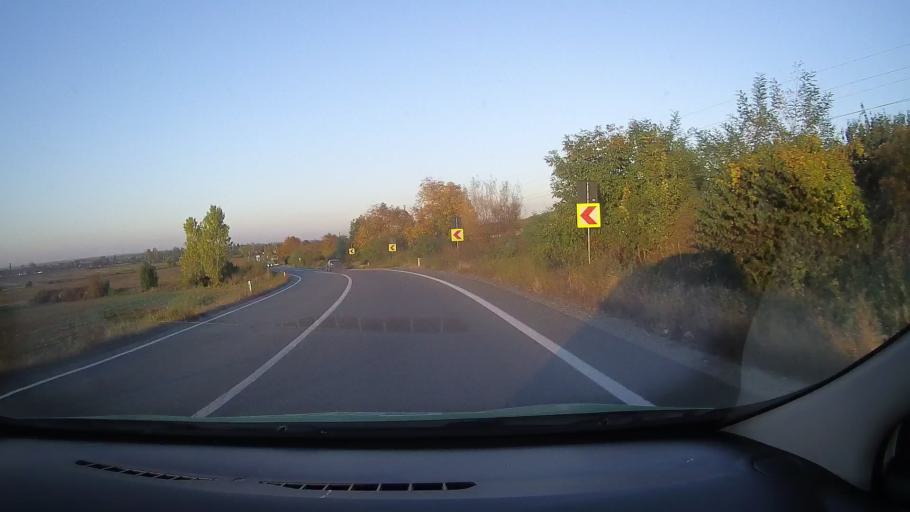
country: RO
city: Dioszeg
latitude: 47.2776
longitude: 21.9831
